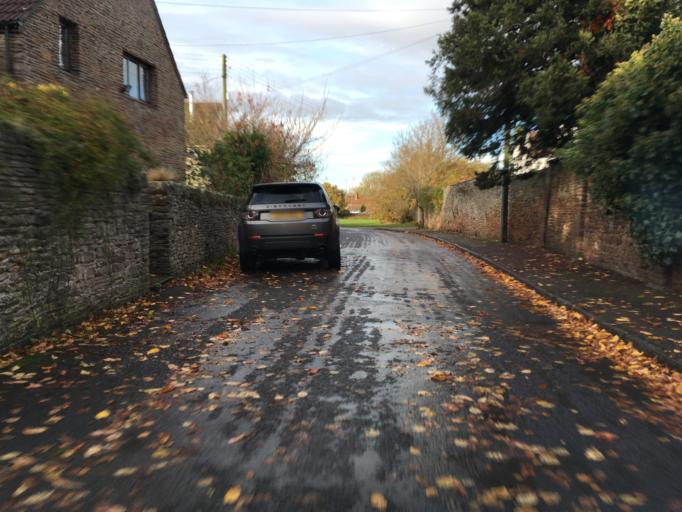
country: GB
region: England
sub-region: South Gloucestershire
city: Tytherington
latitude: 51.5511
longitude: -2.4661
